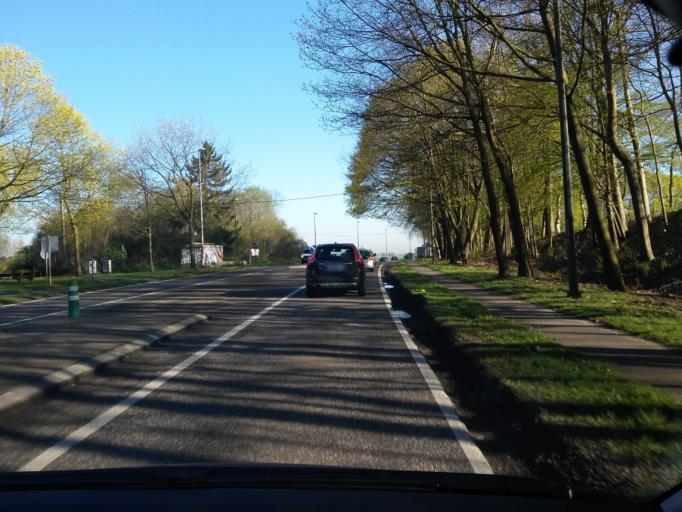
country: BE
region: Wallonia
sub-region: Province du Brabant Wallon
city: Braine-l'Alleud
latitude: 50.6548
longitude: 4.4131
